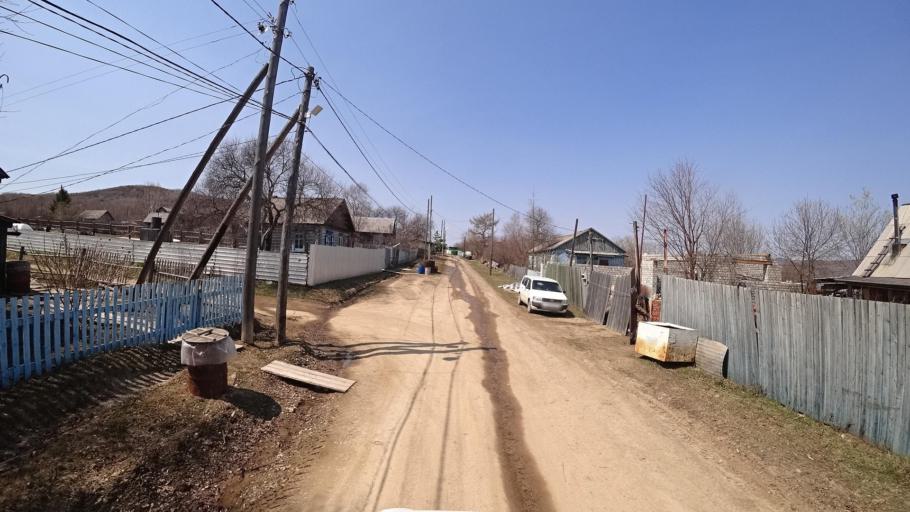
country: RU
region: Khabarovsk Krai
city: Selikhino
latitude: 50.6696
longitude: 137.3988
